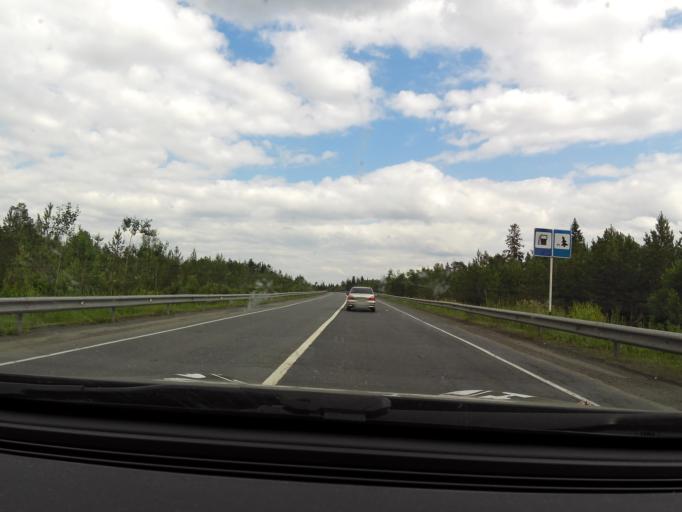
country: RU
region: Sverdlovsk
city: Atig
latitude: 56.7961
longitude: 59.4027
